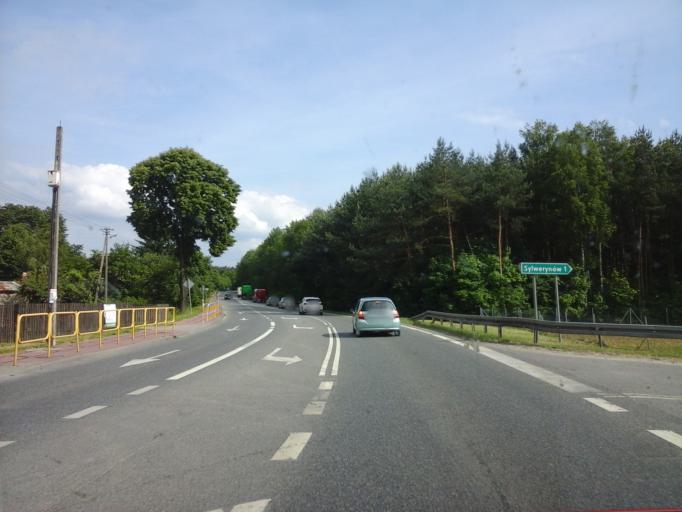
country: PL
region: Lodz Voivodeship
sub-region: Powiat opoczynski
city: Paradyz
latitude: 51.2989
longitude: 20.1193
